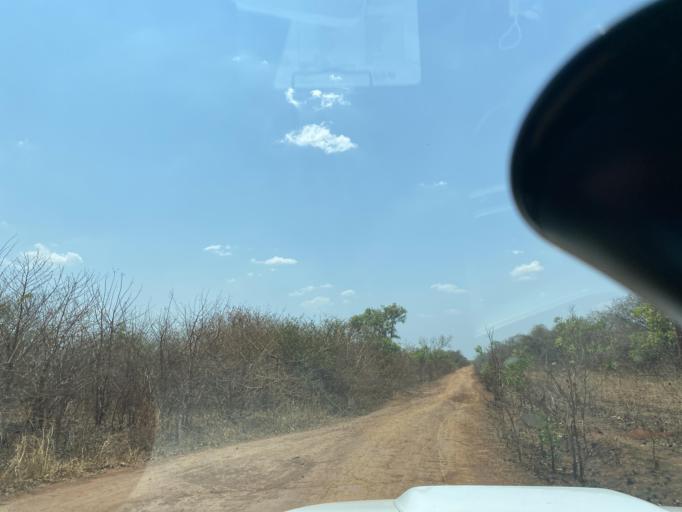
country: ZM
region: Lusaka
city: Lusaka
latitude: -15.5049
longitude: 27.9704
